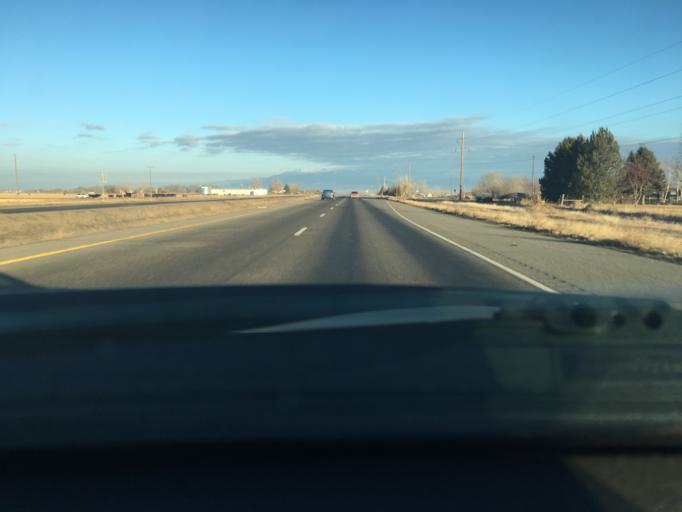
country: US
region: Colorado
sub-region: Montrose County
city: Olathe
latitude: 38.5749
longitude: -107.9616
